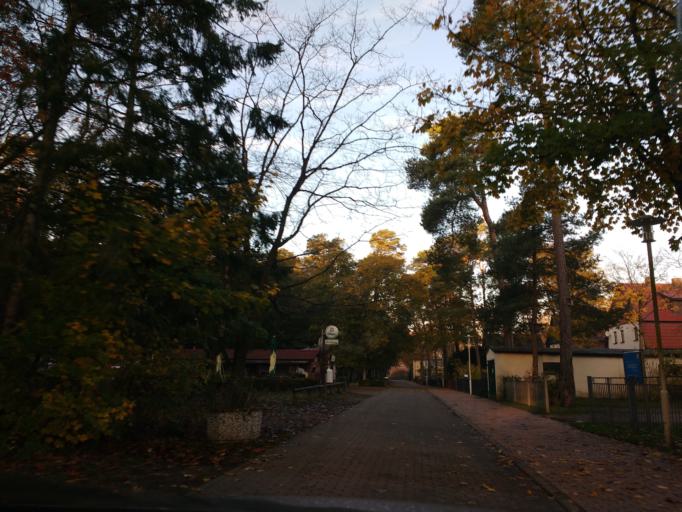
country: DE
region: Mecklenburg-Vorpommern
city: Ostseebad Boltenhagen
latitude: 53.9818
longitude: 11.2245
